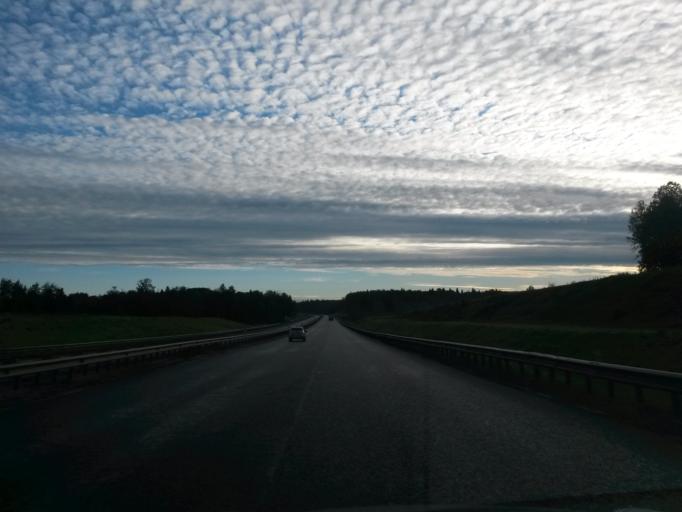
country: RU
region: Vladimir
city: Strunino
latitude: 56.5360
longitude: 38.5824
